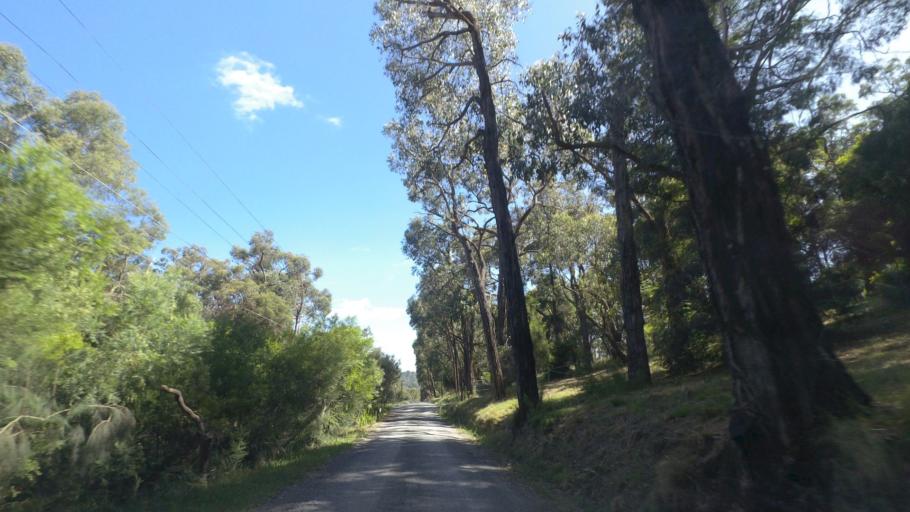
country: AU
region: Victoria
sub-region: Yarra Ranges
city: Kalorama
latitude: -37.8049
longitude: 145.3710
